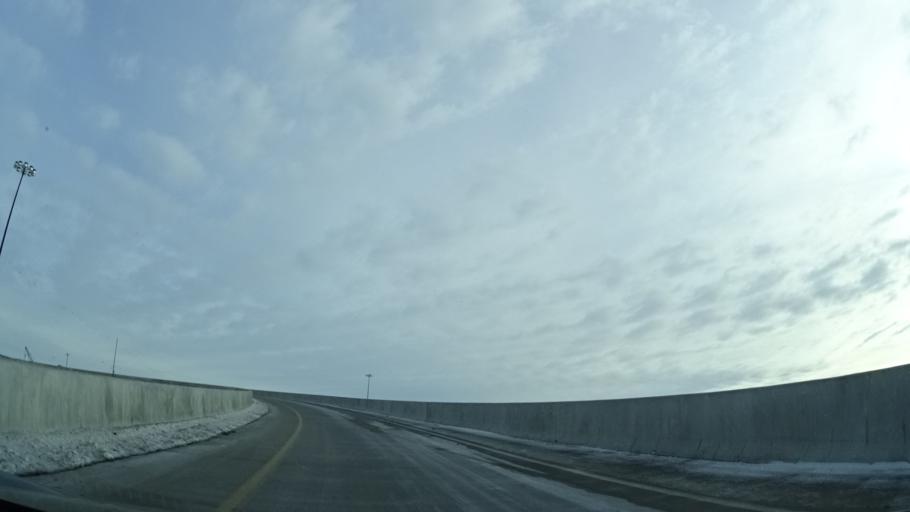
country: US
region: Iowa
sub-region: Pottawattamie County
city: Council Bluffs
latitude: 41.2312
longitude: -95.8978
